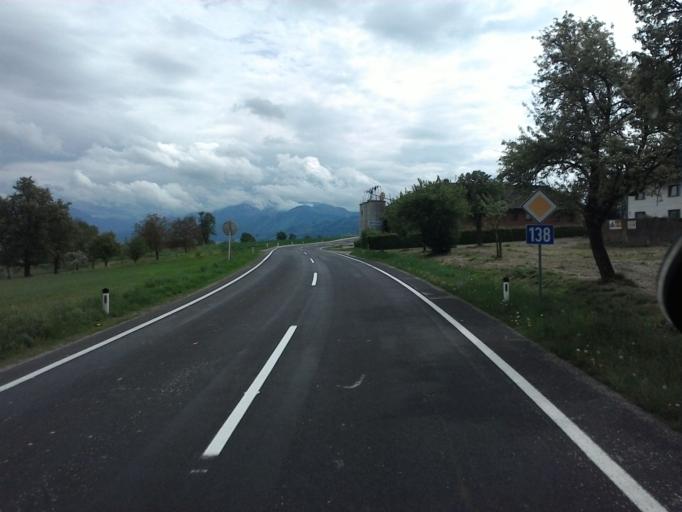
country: AT
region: Upper Austria
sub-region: Politischer Bezirk Kirchdorf an der Krems
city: Kremsmunster
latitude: 47.9758
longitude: 14.0786
